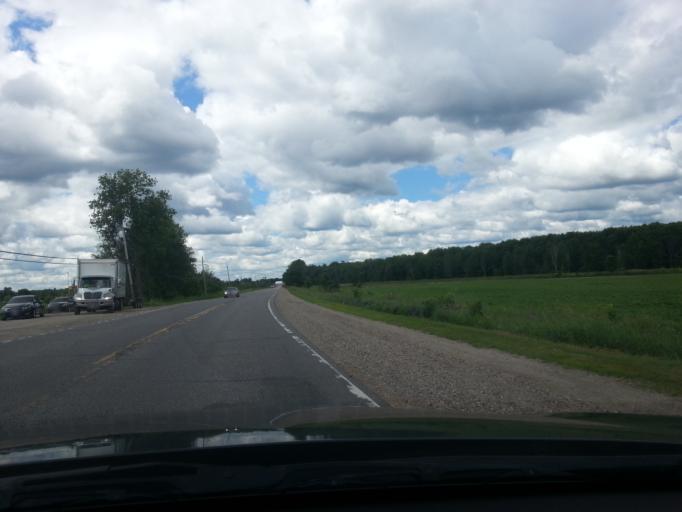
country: CA
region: Ontario
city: Perth
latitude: 44.6620
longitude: -76.2423
